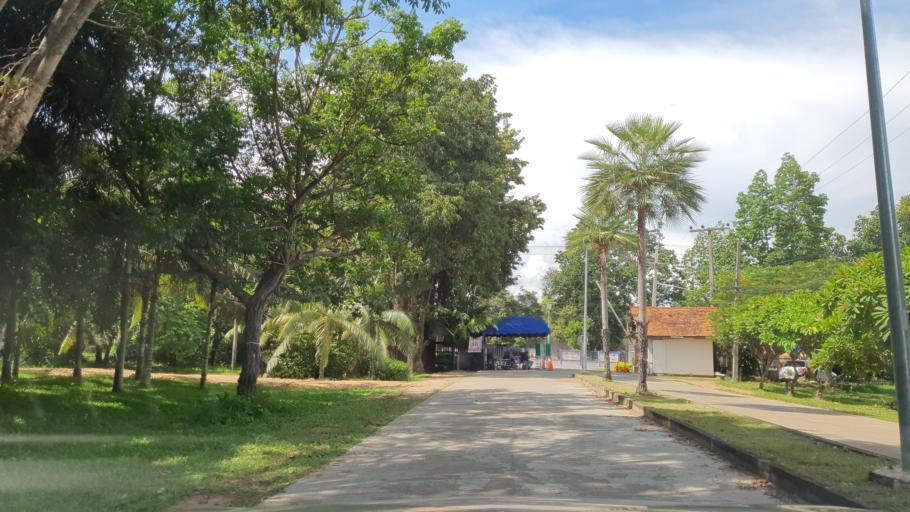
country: TH
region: Chiang Mai
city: San Pa Tong
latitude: 18.5934
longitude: 98.8750
